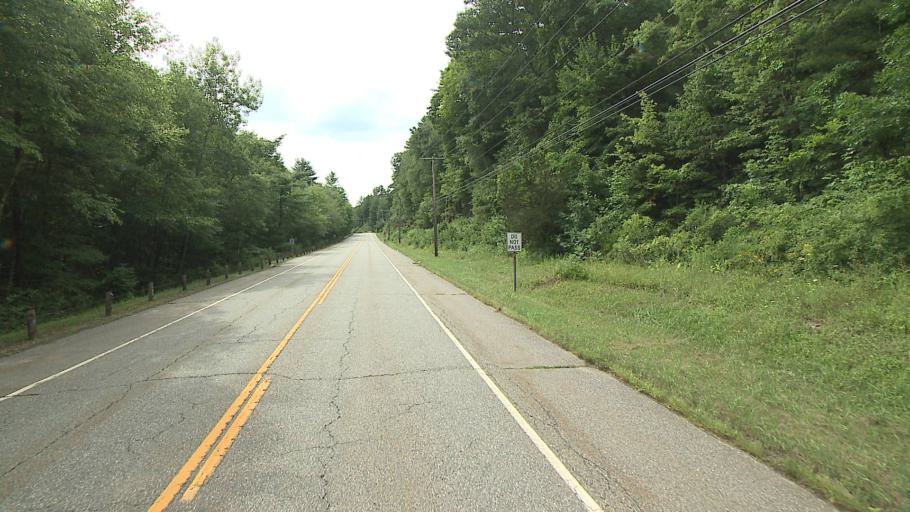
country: US
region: Connecticut
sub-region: Litchfield County
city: New Preston
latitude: 41.6717
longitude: -73.3242
